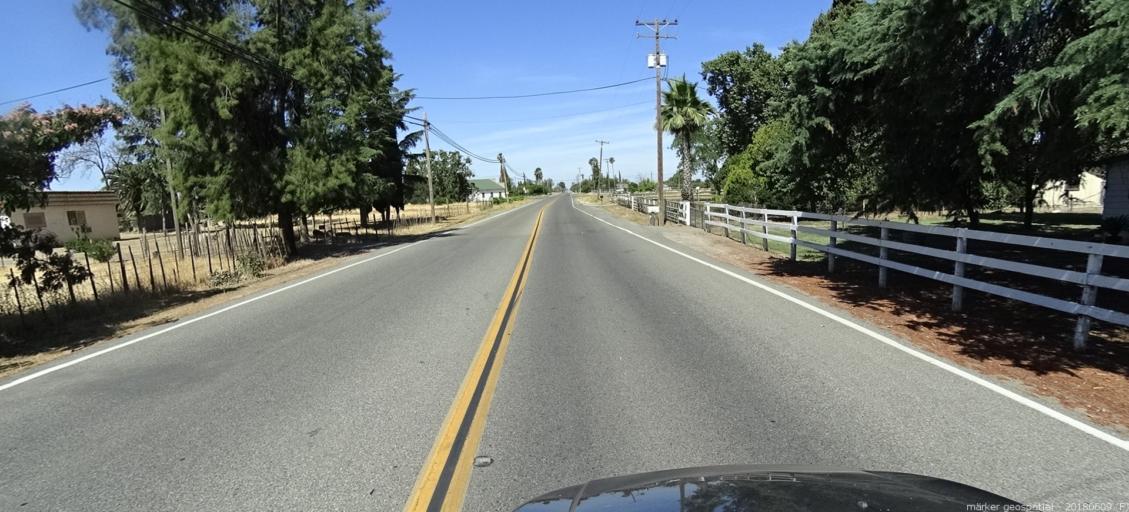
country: US
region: California
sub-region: Madera County
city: Madera
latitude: 36.9529
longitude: -120.1081
